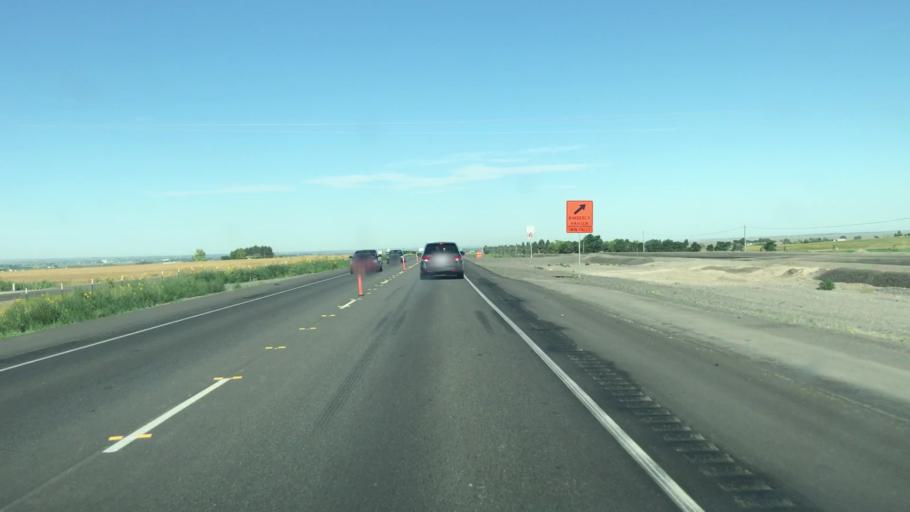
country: US
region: Idaho
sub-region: Twin Falls County
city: Hansen
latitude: 42.5762
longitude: -114.2687
